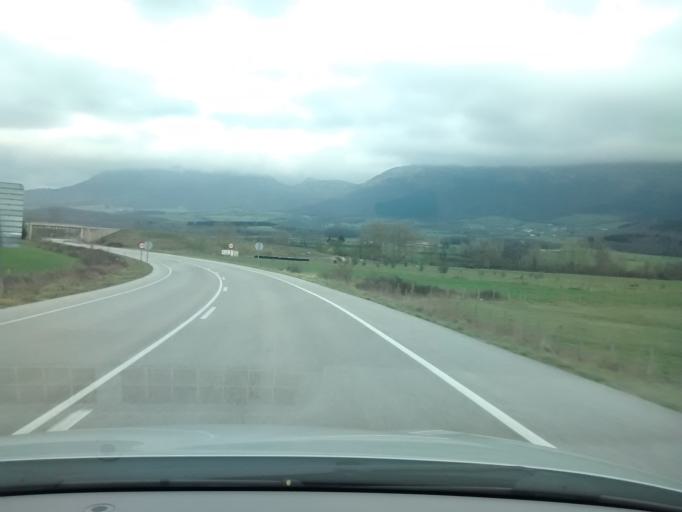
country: ES
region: Castille and Leon
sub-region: Provincia de Burgos
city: Villasana de Mena
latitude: 43.0946
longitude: -3.3041
